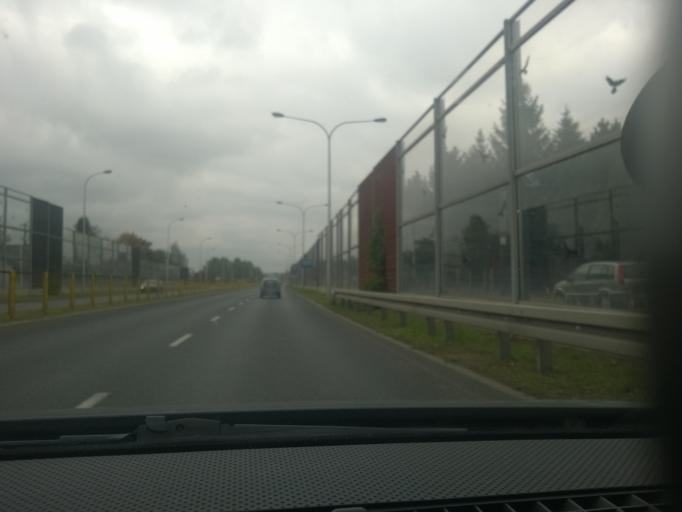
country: PL
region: Greater Poland Voivodeship
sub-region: Kalisz
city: Kalisz
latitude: 51.7459
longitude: 18.0810
